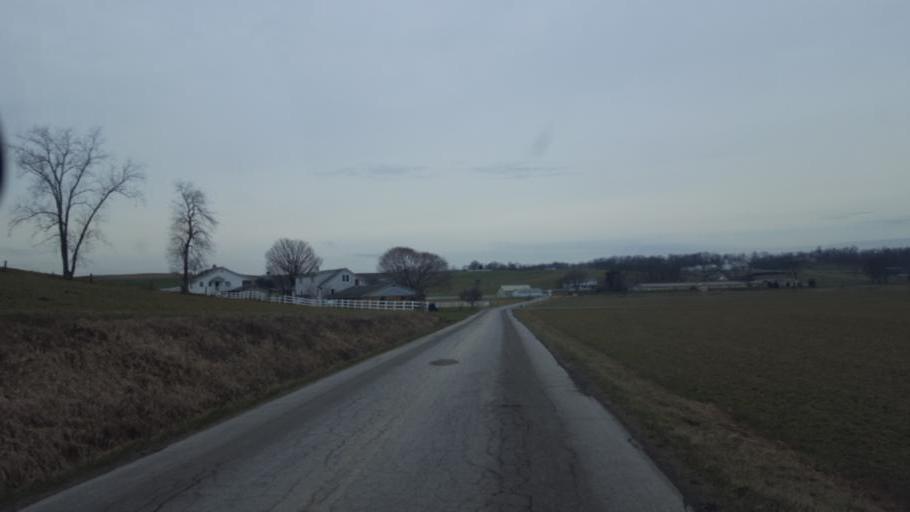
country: US
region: Ohio
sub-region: Tuscarawas County
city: Sugarcreek
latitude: 40.5136
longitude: -81.7343
